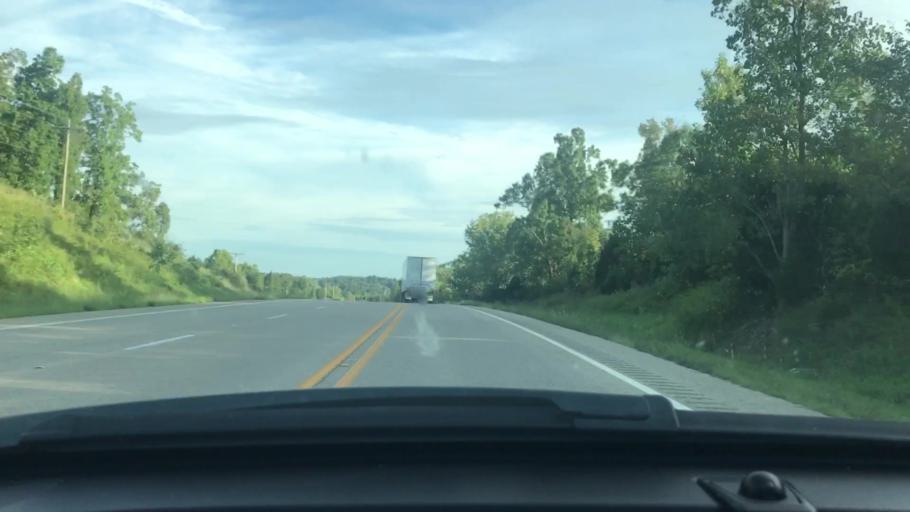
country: US
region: Arkansas
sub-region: Lawrence County
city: Hoxie
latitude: 36.1486
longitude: -91.1602
